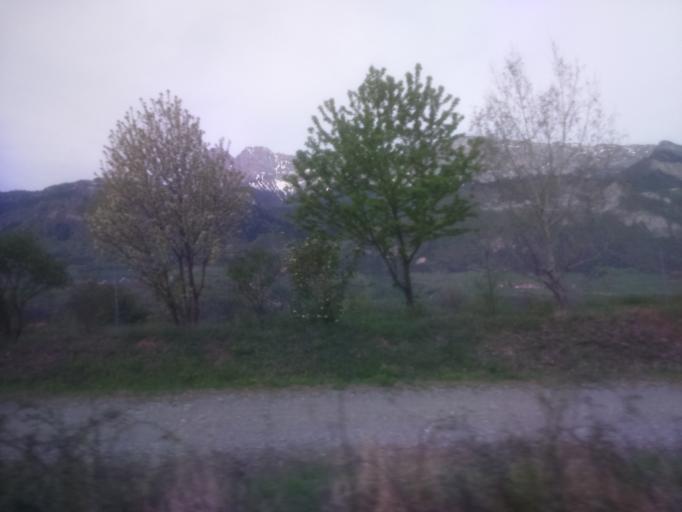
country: FR
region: Rhone-Alpes
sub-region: Departement de l'Isere
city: Le Gua
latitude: 45.0052
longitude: 5.6563
